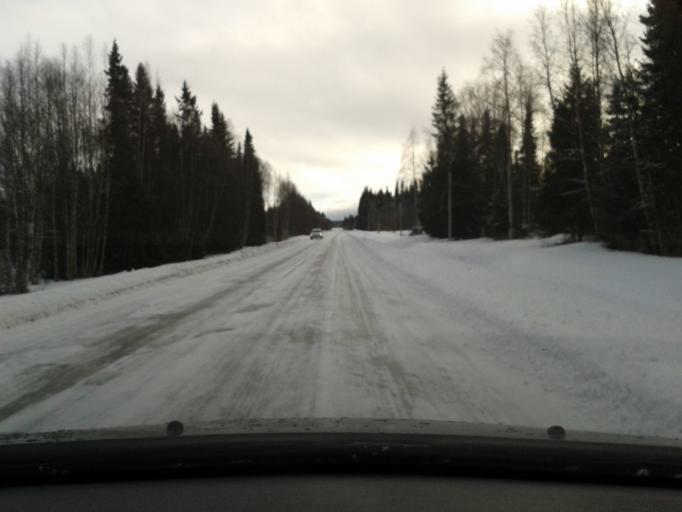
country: SE
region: Vaesterbotten
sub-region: Vilhelmina Kommun
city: Sjoberg
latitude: 64.7207
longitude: 16.2327
